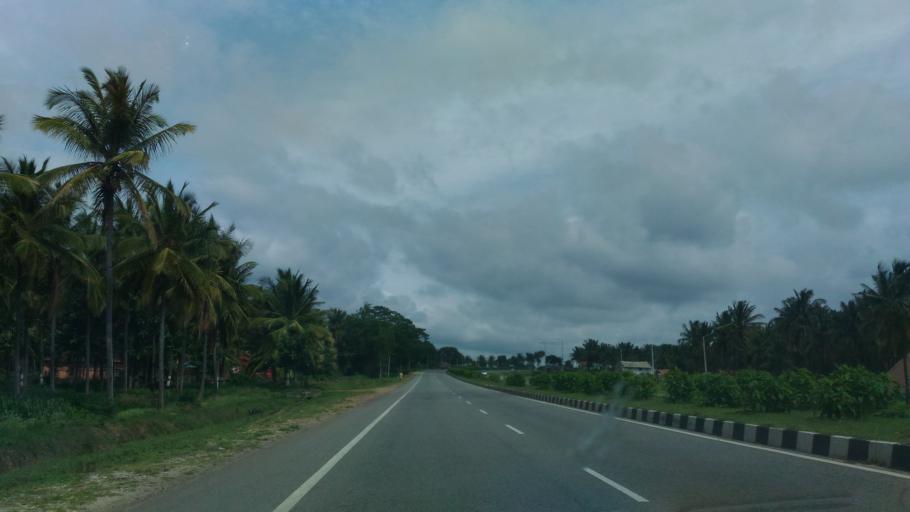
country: IN
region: Karnataka
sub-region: Hassan
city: Channarayapatna
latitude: 12.9430
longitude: 76.3428
